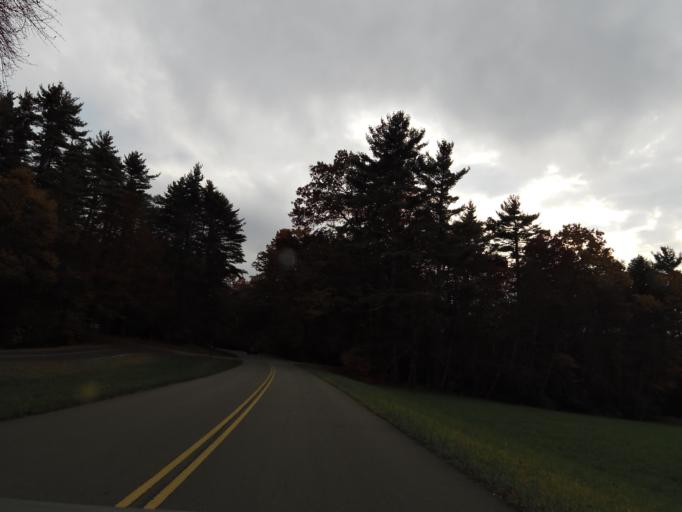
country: US
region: North Carolina
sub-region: Ashe County
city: Jefferson
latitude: 36.3586
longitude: -81.3727
